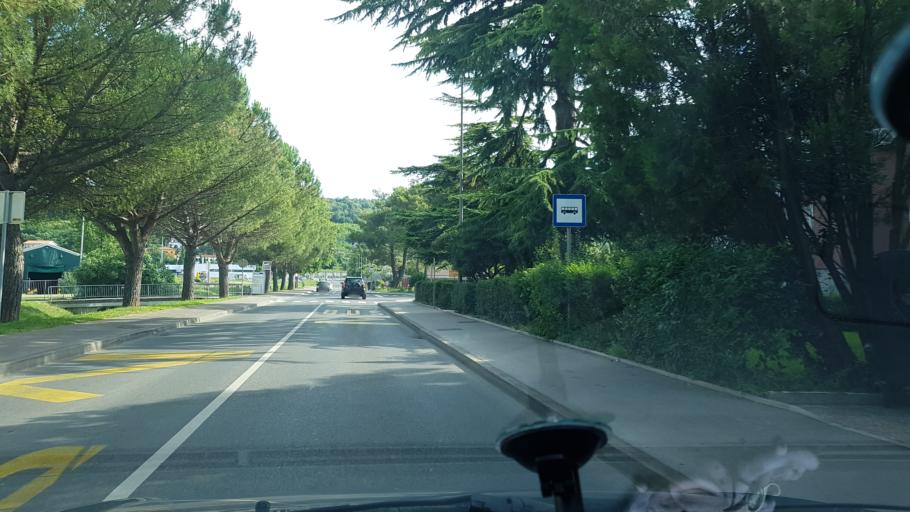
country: SI
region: Koper-Capodistria
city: Koper
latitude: 45.5343
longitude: 13.7286
